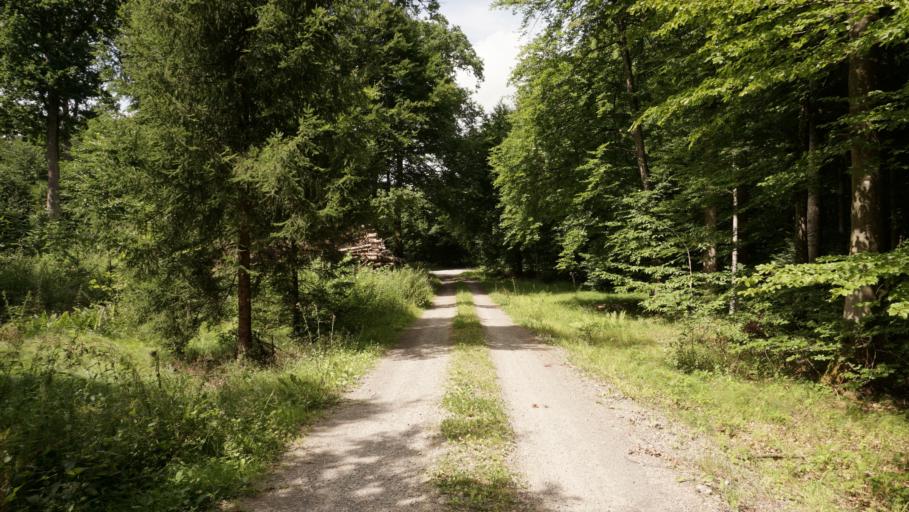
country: DE
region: Baden-Wuerttemberg
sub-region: Karlsruhe Region
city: Mosbach
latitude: 49.3263
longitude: 9.1923
